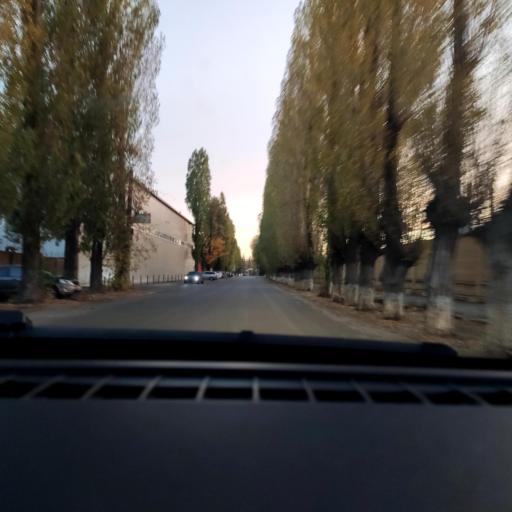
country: RU
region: Voronezj
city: Voronezh
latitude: 51.6494
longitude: 39.2790
